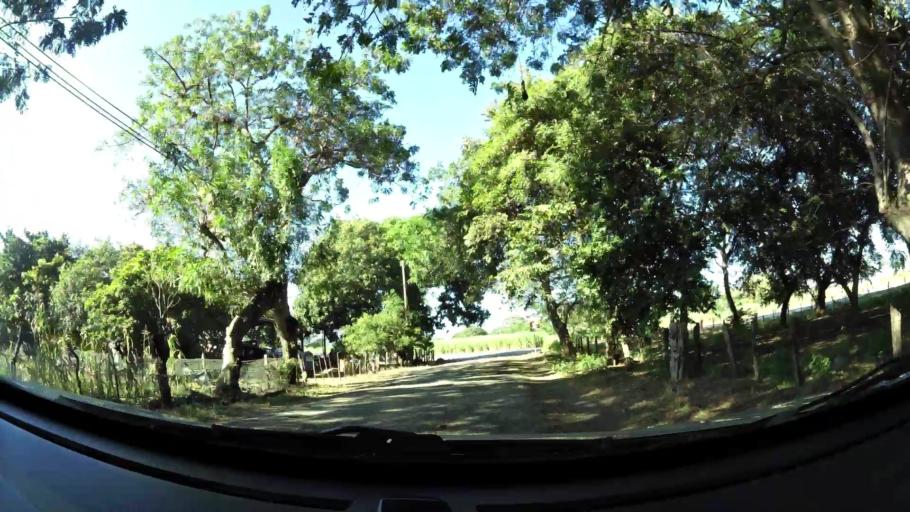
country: CR
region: Guanacaste
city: Belen
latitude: 10.4426
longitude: -85.5556
